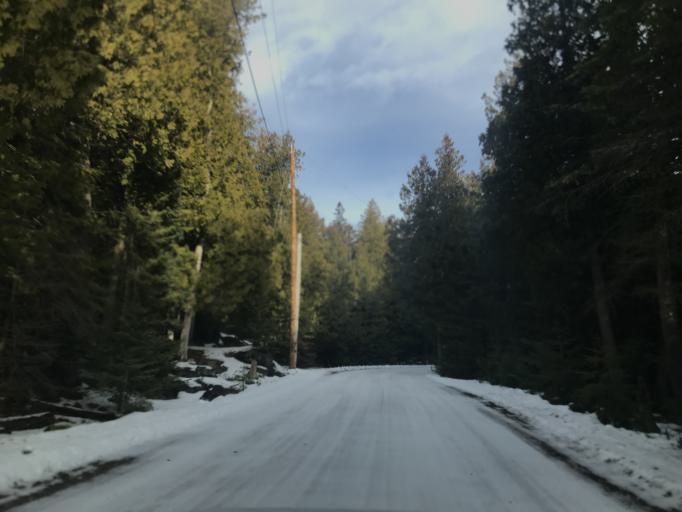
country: US
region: Wisconsin
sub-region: Door County
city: Sturgeon Bay
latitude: 45.1380
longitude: -87.0456
